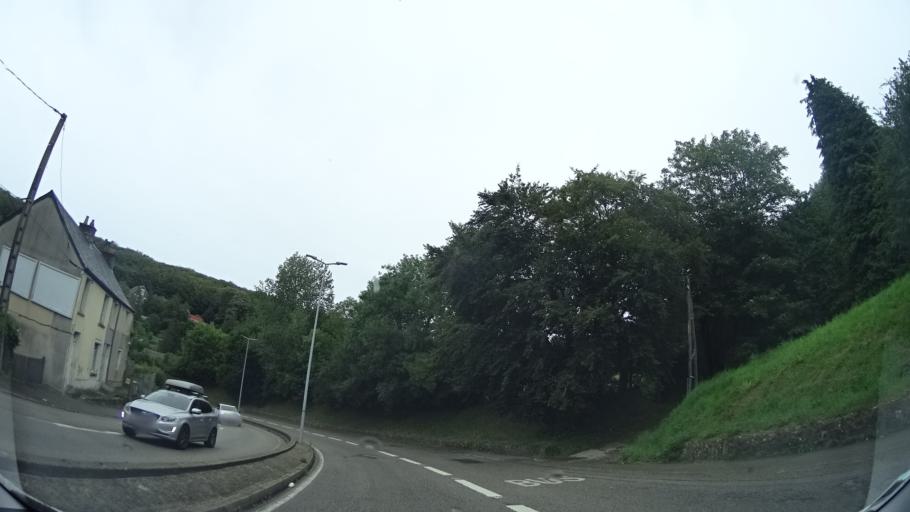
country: FR
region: Lower Normandy
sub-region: Departement de la Manche
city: Cherbourg-Octeville
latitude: 49.6223
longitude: -1.6126
